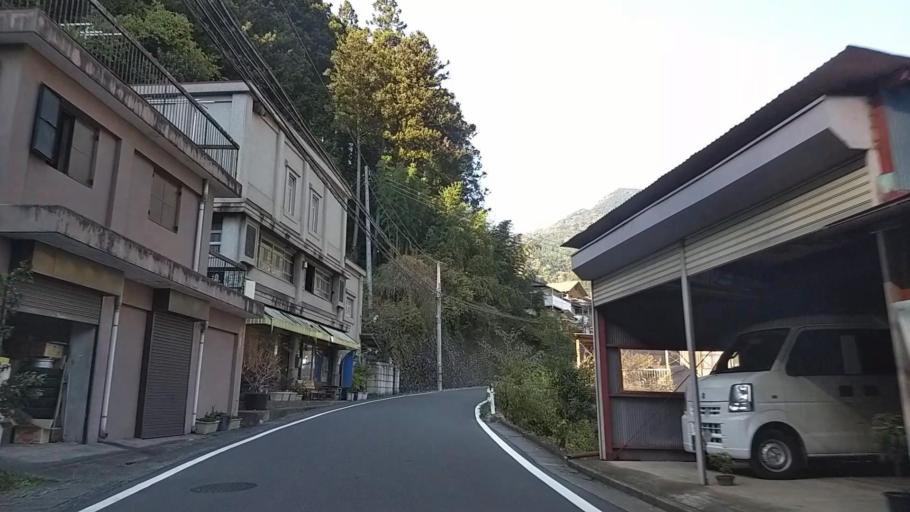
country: JP
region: Tokyo
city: Itsukaichi
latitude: 35.8096
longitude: 139.0948
